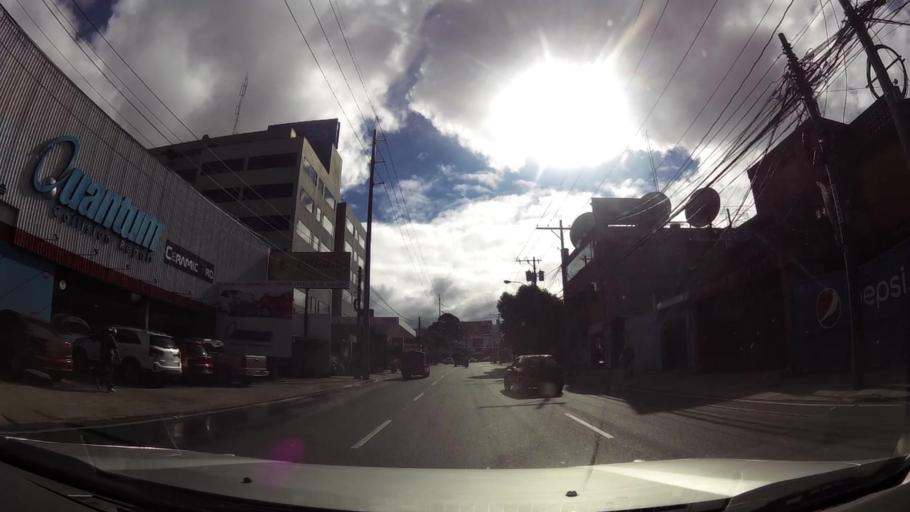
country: GT
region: Guatemala
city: Santa Catarina Pinula
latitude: 14.5871
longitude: -90.5031
